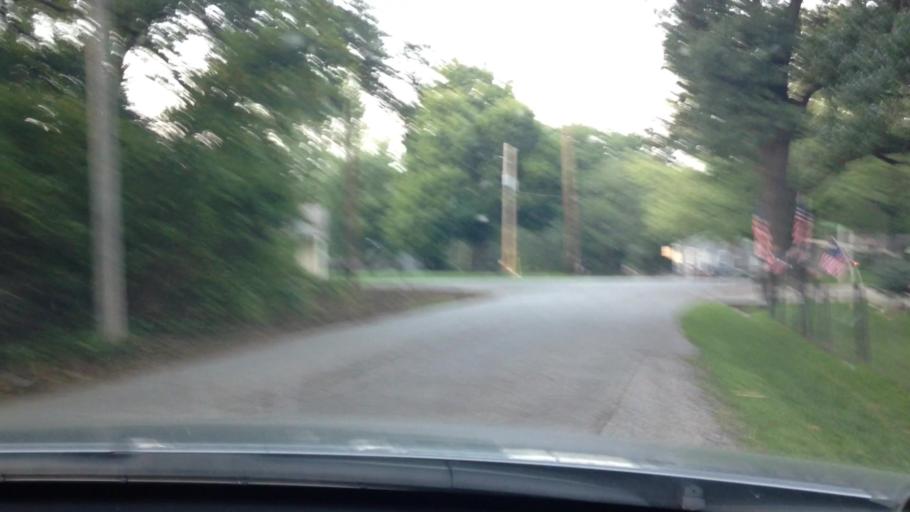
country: US
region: Missouri
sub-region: Clay County
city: Claycomo
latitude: 39.1880
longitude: -94.5118
